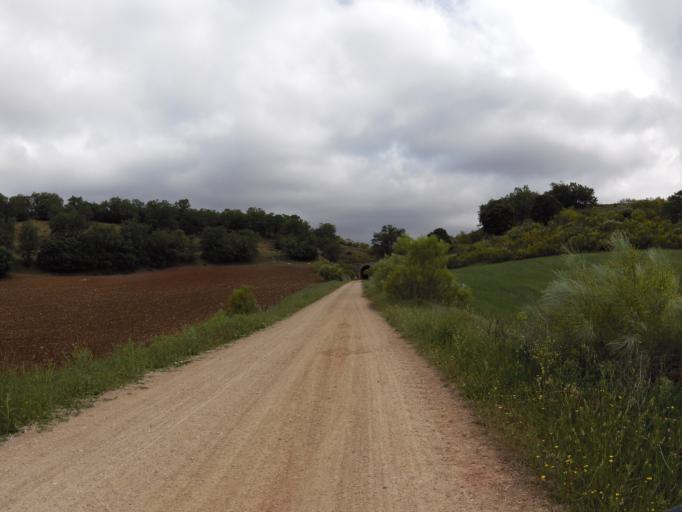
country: ES
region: Castille-La Mancha
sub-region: Provincia de Albacete
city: Robledo
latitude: 38.7255
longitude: -2.4780
